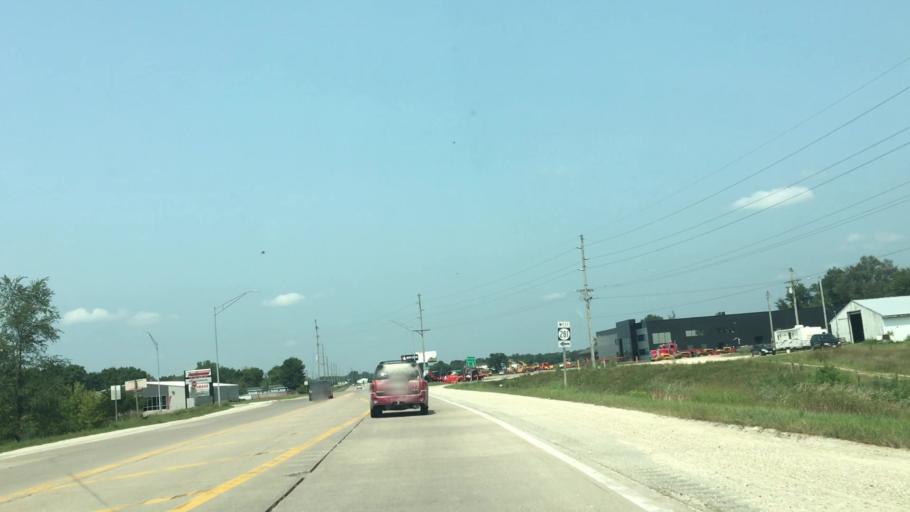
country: US
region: Iowa
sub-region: Fayette County
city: Oelwein
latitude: 42.6411
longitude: -91.9085
